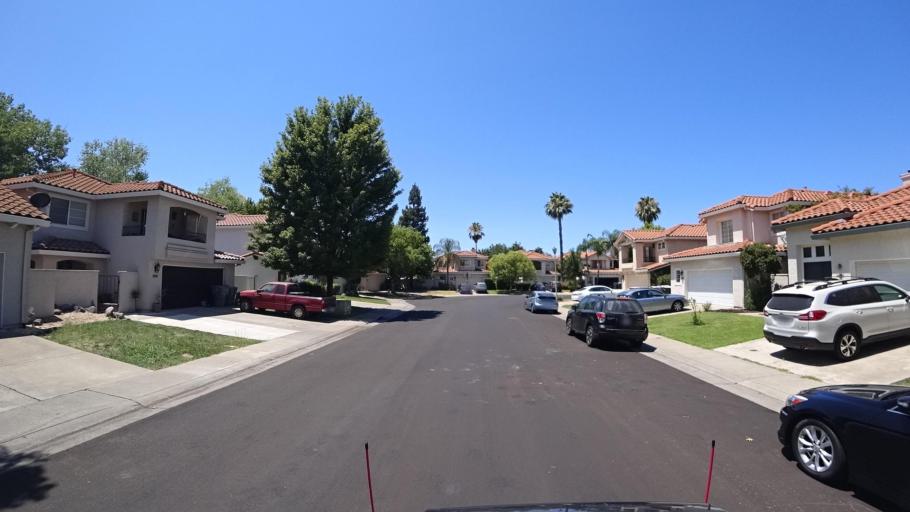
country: US
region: California
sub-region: Placer County
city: Rocklin
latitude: 38.8170
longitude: -121.2626
